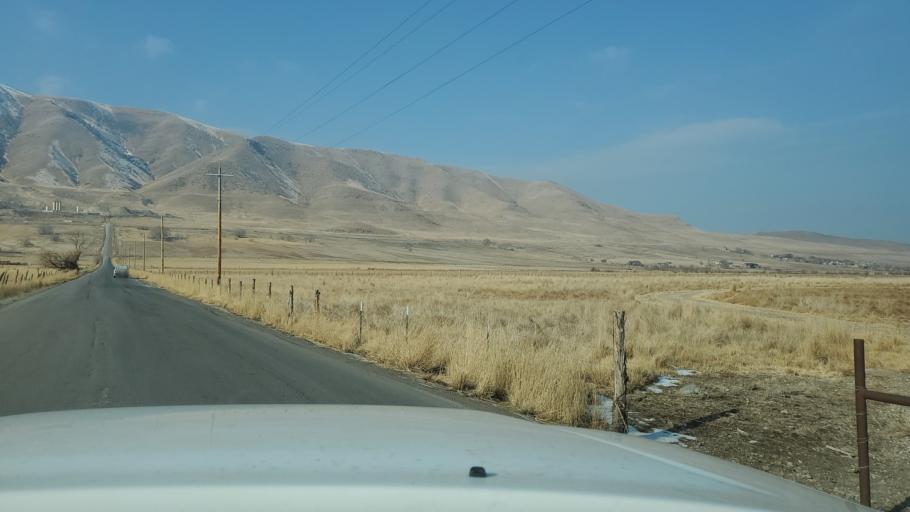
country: US
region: Utah
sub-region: Utah County
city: West Mountain
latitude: 40.0997
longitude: -111.7879
